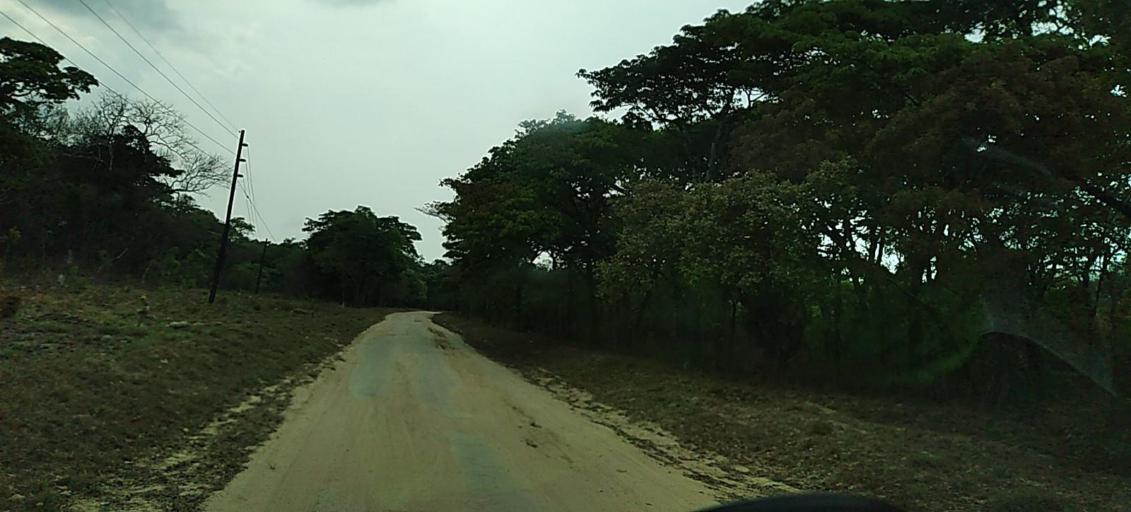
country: ZM
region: North-Western
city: Solwezi
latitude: -12.7663
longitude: 26.4640
